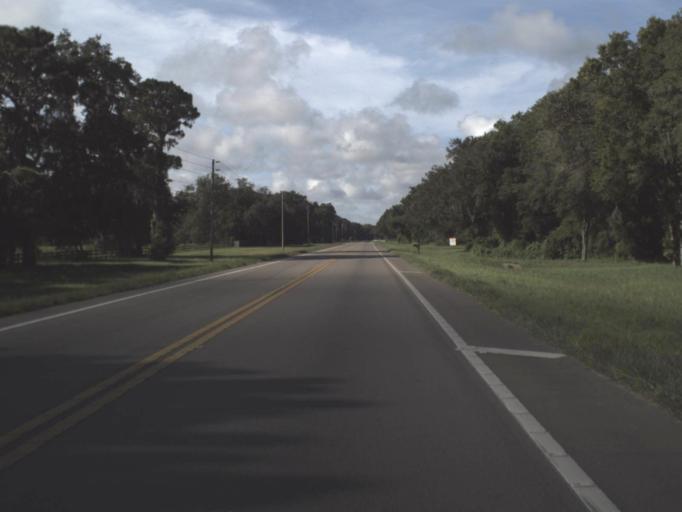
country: US
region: Florida
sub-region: Pasco County
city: Shady Hills
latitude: 28.3891
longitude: -82.4890
